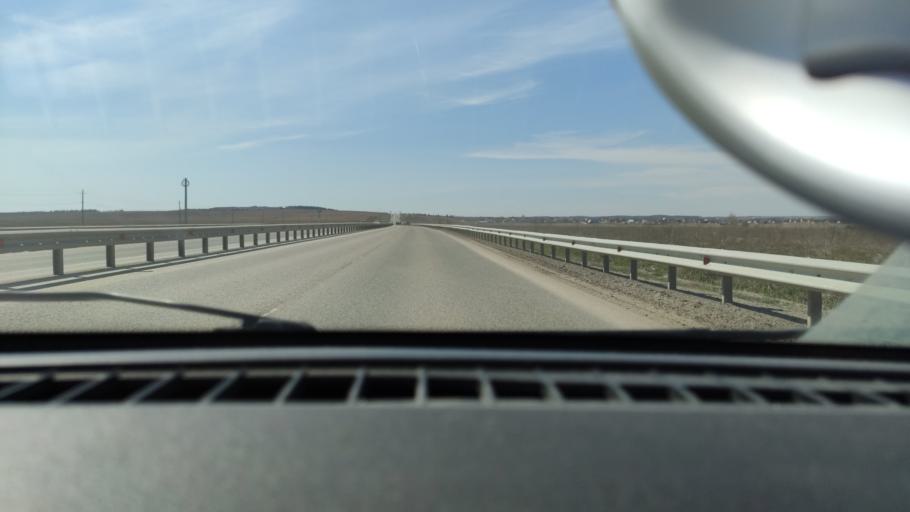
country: RU
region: Perm
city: Kultayevo
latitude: 57.8826
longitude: 55.9199
